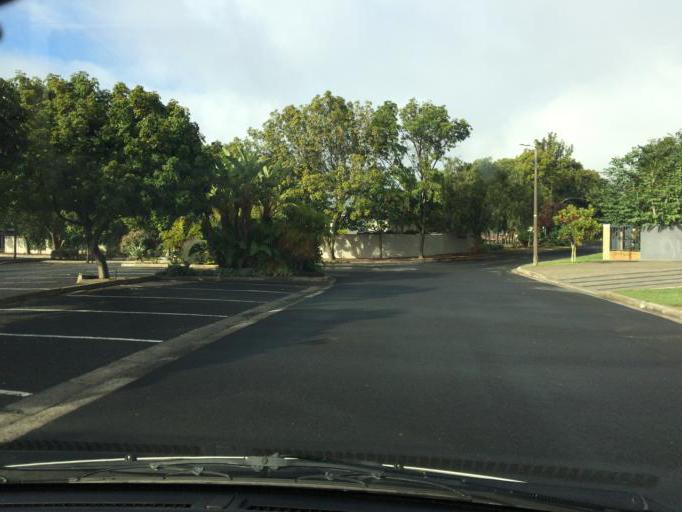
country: ZA
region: Western Cape
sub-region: City of Cape Town
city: Kraaifontein
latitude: -33.8659
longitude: 18.6509
